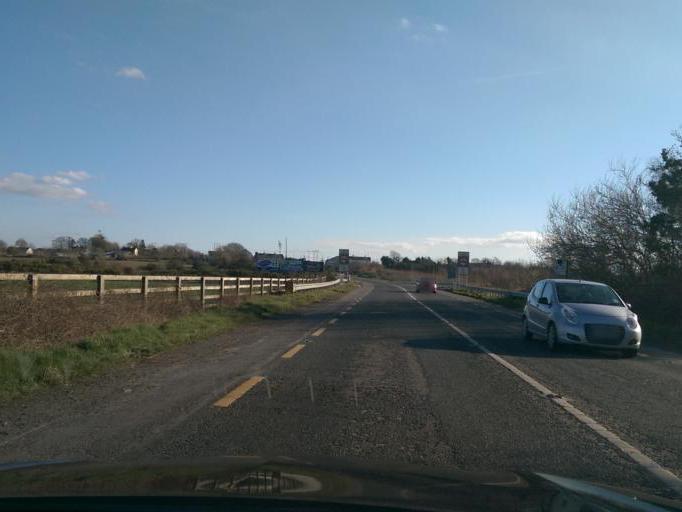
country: IE
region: Connaught
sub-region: County Galway
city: Oranmore
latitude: 53.2152
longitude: -8.8716
